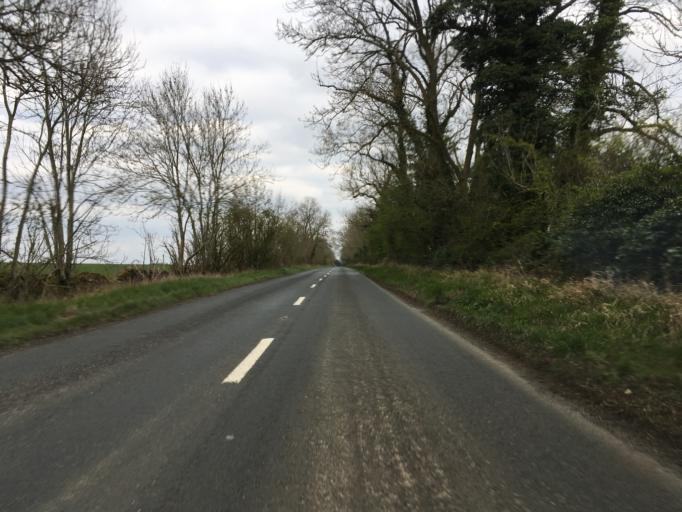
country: GB
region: England
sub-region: Gloucestershire
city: Bourton on the Water
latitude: 51.7891
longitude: -1.7321
